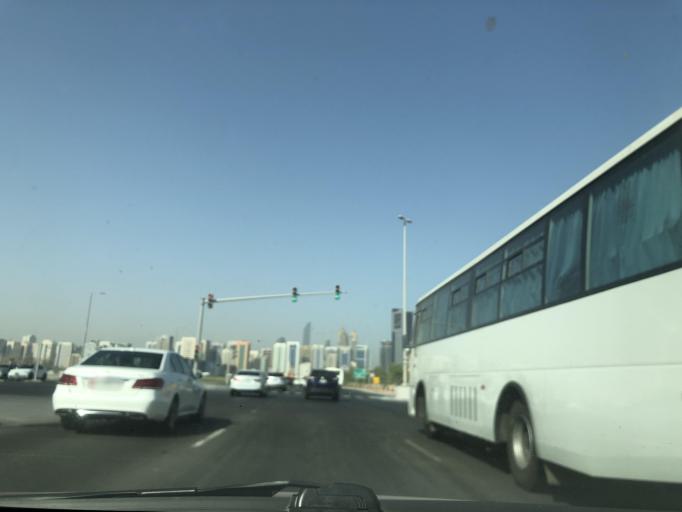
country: AE
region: Abu Dhabi
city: Abu Dhabi
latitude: 24.5115
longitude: 54.3855
